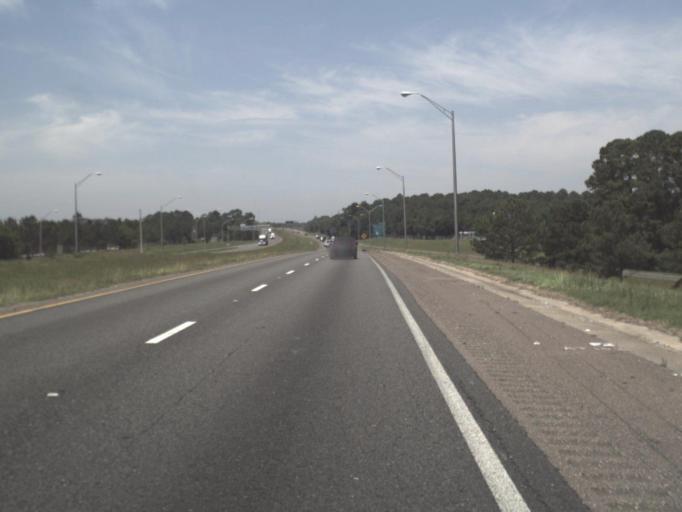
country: US
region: Florida
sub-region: Duval County
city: Jacksonville
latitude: 30.3416
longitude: -81.5424
